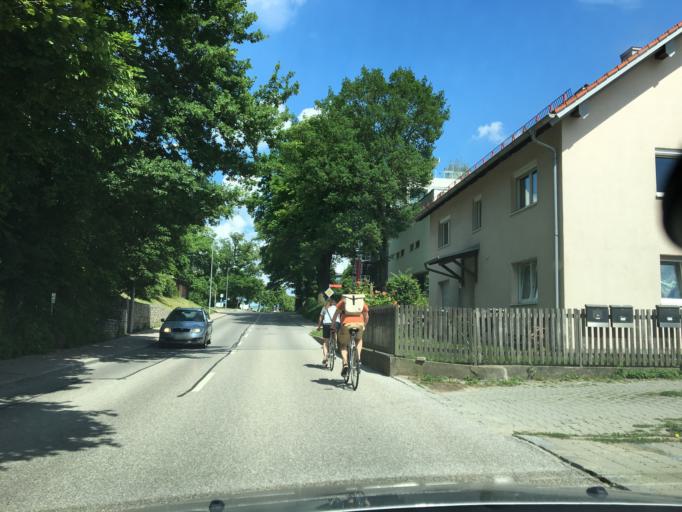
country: DE
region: Bavaria
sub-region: Upper Bavaria
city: Freising
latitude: 48.3973
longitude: 11.7213
